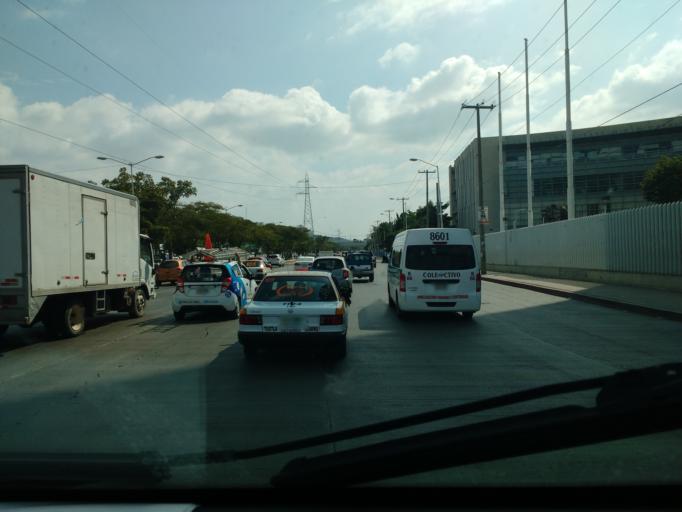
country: MX
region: Chiapas
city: Tuxtla Gutierrez
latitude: 16.7553
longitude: -93.0809
